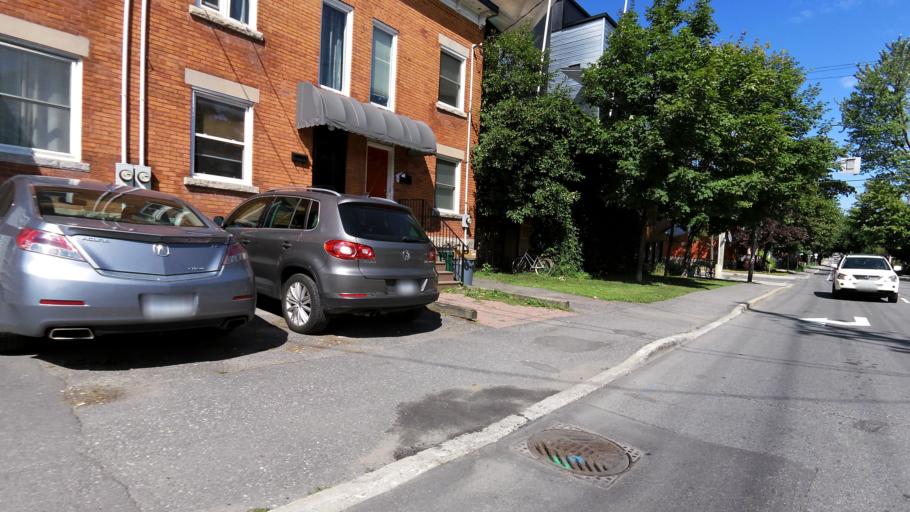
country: CA
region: Ontario
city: Ottawa
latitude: 45.4082
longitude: -75.6962
